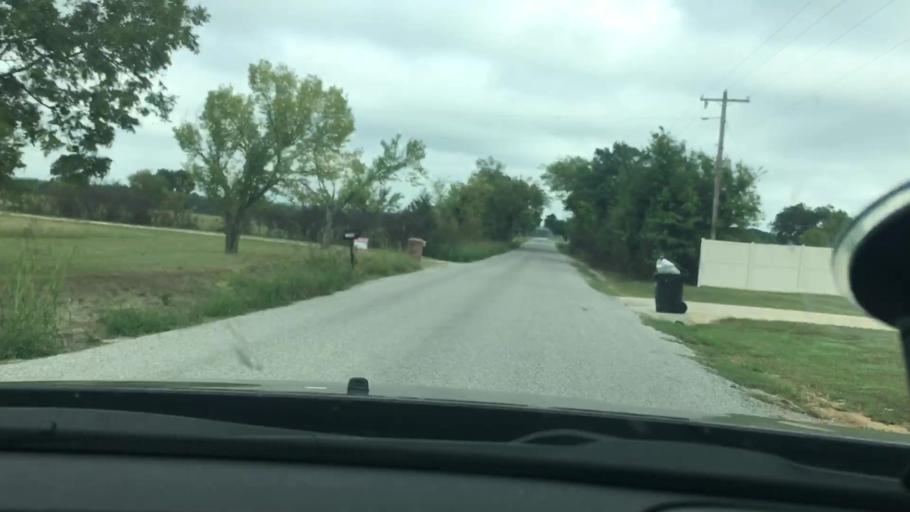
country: US
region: Oklahoma
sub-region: Carter County
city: Lone Grove
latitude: 34.1270
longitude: -97.2128
